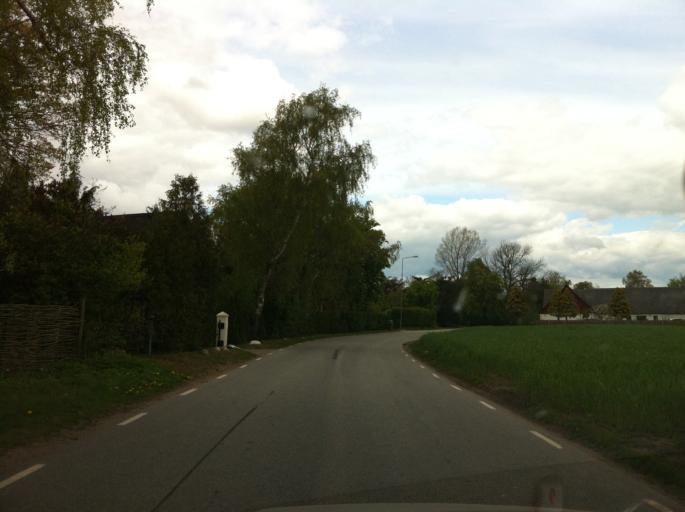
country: SE
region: Skane
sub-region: Kavlinge Kommun
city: Loddekopinge
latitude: 55.8048
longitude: 13.0399
